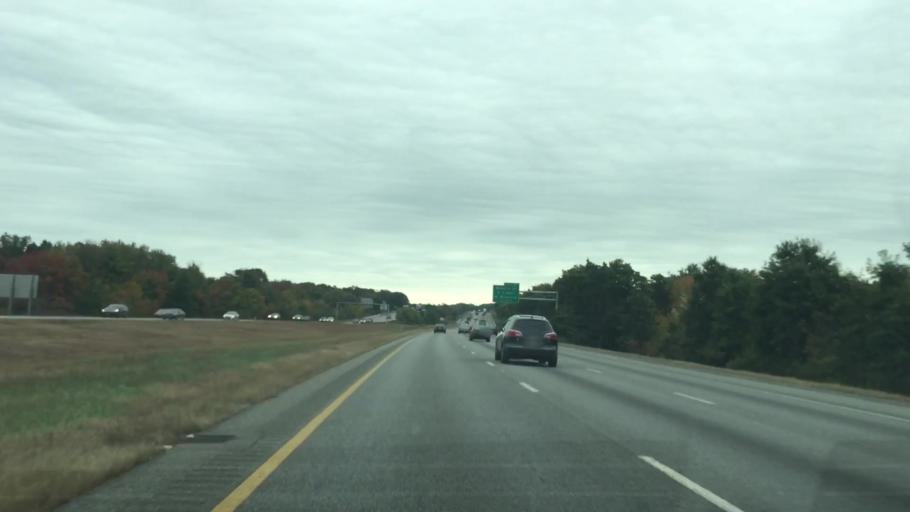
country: US
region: Massachusetts
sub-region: Middlesex County
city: Lowell
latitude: 42.6143
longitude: -71.3008
